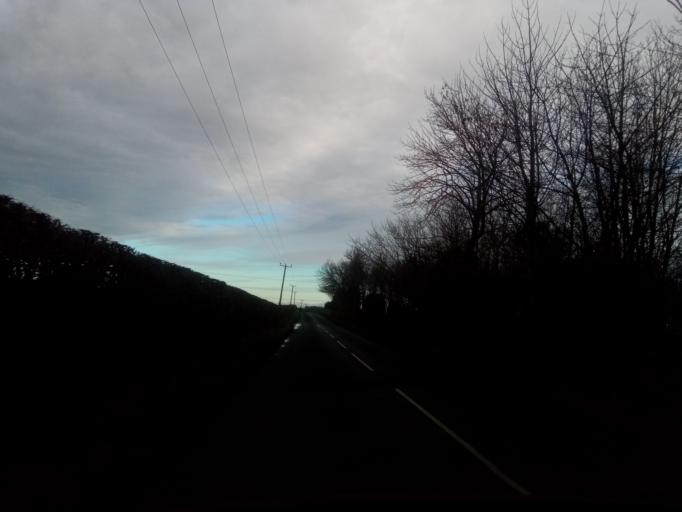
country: GB
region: Scotland
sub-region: The Scottish Borders
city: Coldstream
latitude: 55.6629
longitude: -2.2319
